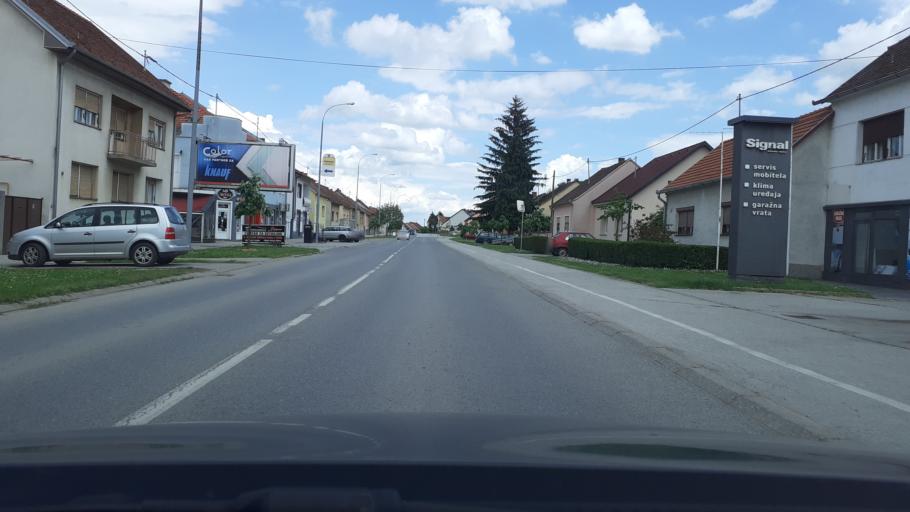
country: HR
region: Pozesko-Slavonska
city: Pozega
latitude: 45.3339
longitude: 17.6969
